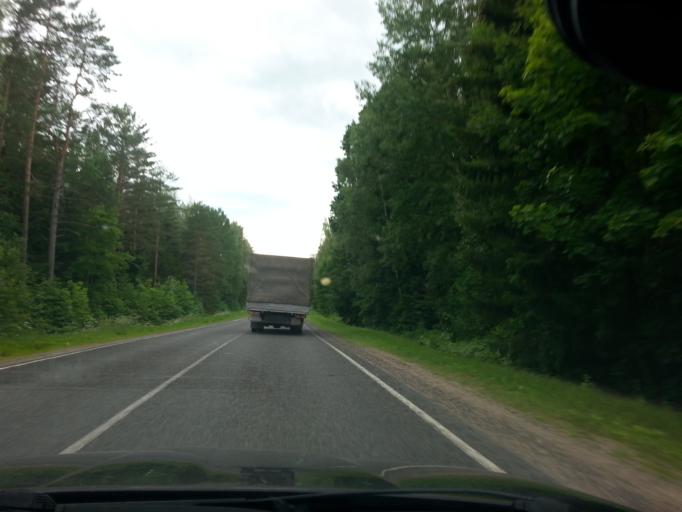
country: BY
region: Minsk
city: Svir
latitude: 54.8553
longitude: 26.3022
